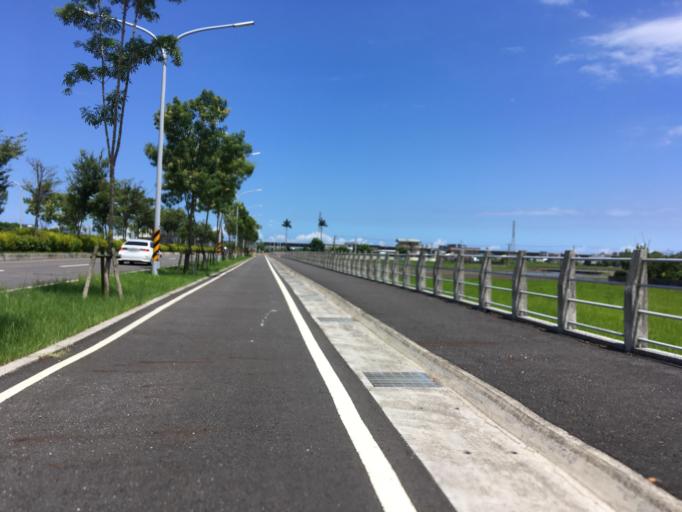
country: TW
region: Taiwan
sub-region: Yilan
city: Yilan
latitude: 24.6934
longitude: 121.7841
